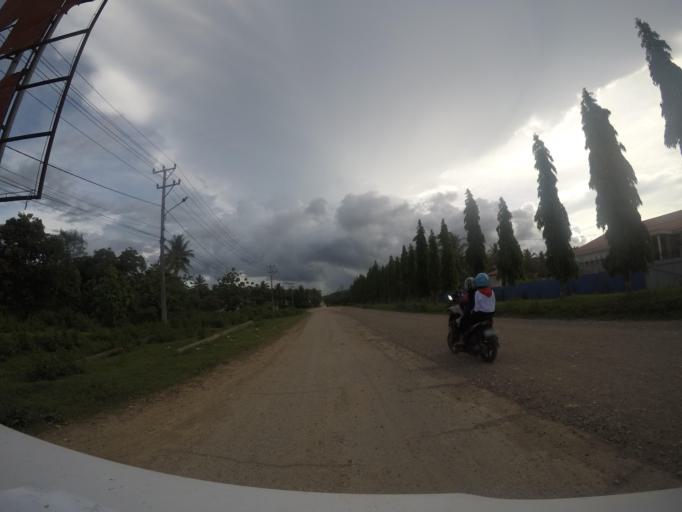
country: TL
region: Lautem
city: Lospalos
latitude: -8.4960
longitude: 126.9919
